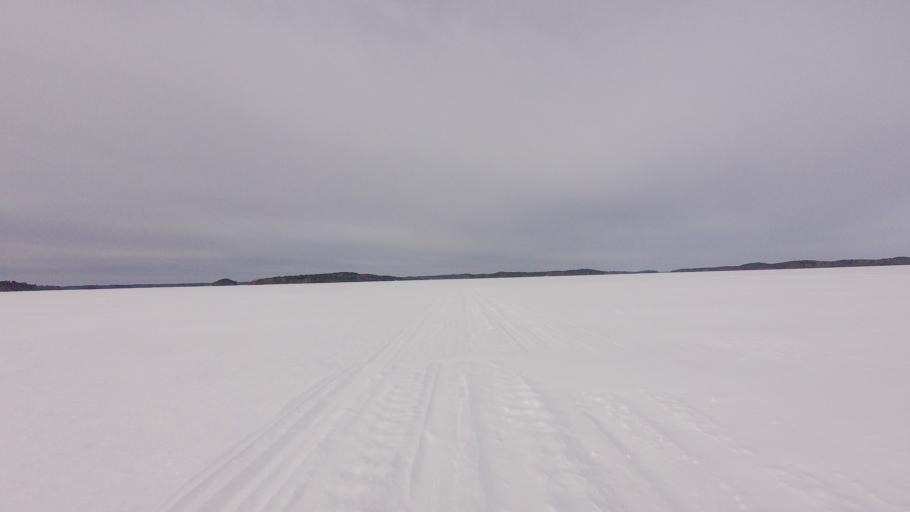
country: FI
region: Southern Savonia
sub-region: Savonlinna
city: Rantasalmi
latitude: 62.1073
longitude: 28.4078
